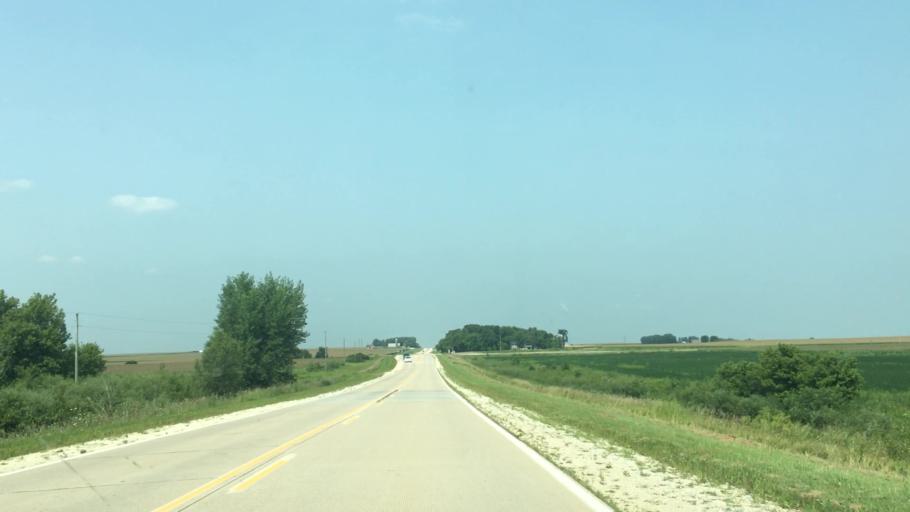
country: US
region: Iowa
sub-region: Fayette County
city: Fayette
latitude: 42.7556
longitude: -91.8043
